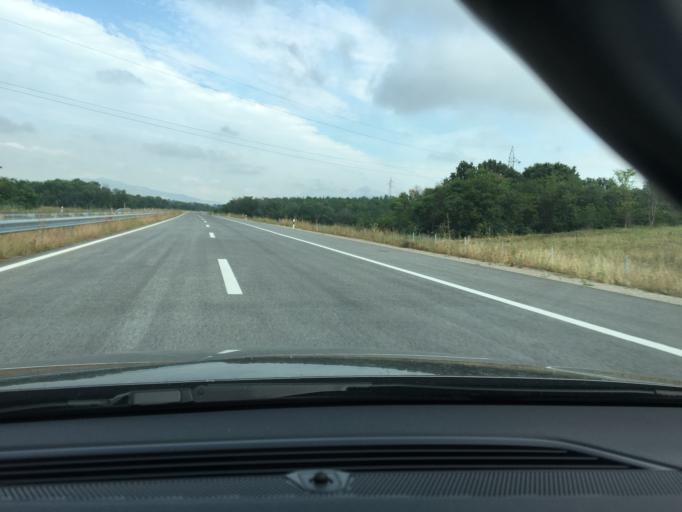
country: MK
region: Sveti Nikole
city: Sveti Nikole
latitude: 41.8454
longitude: 21.9749
